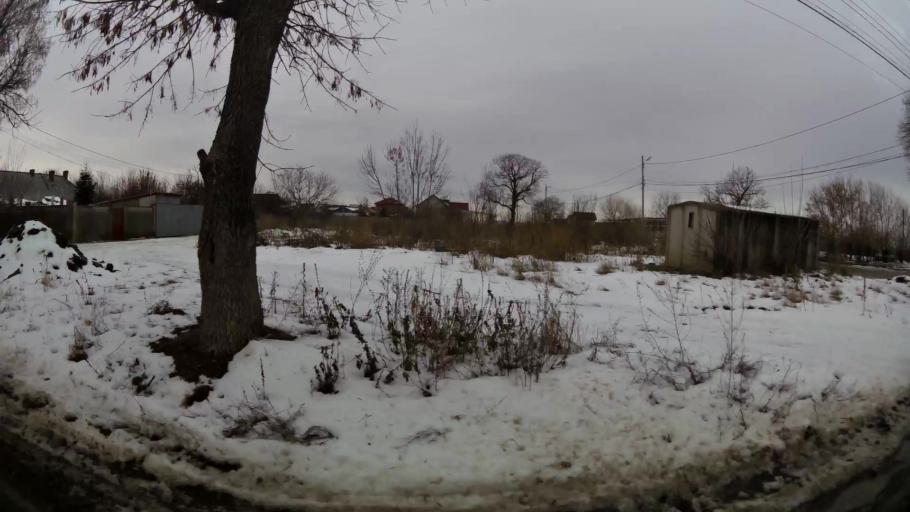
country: RO
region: Ilfov
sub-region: Comuna Pantelimon
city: Pantelimon
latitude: 44.4662
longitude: 26.2088
